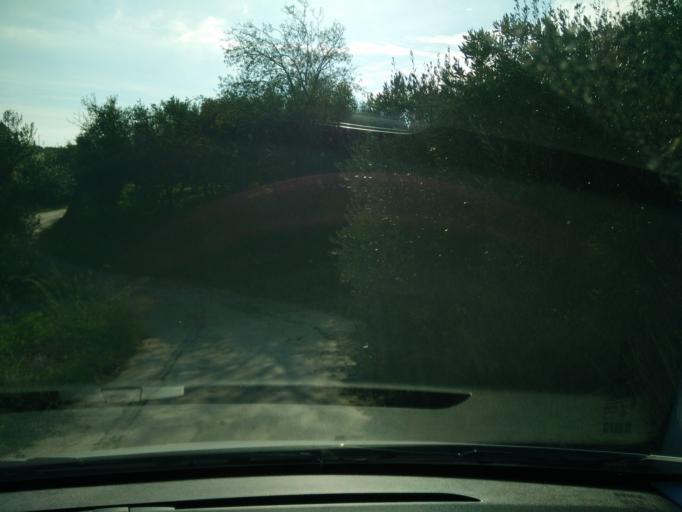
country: GR
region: Crete
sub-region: Nomos Lasithiou
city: Gra Liyia
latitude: 35.0279
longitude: 25.5690
